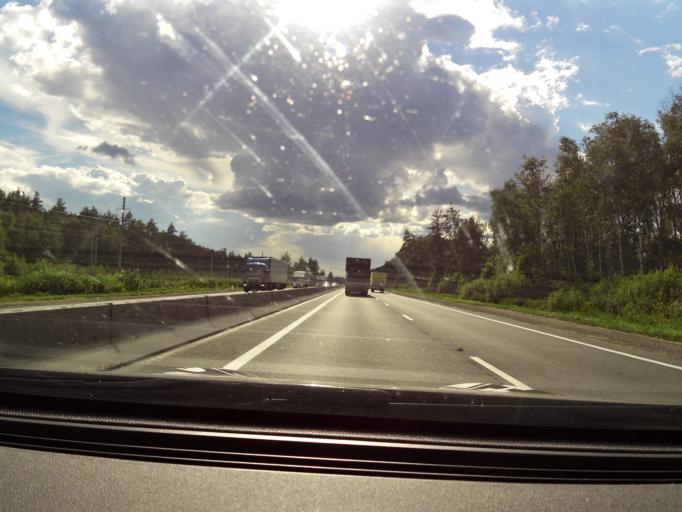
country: RU
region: Nizjnij Novgorod
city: Pyra
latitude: 56.2910
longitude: 43.2987
